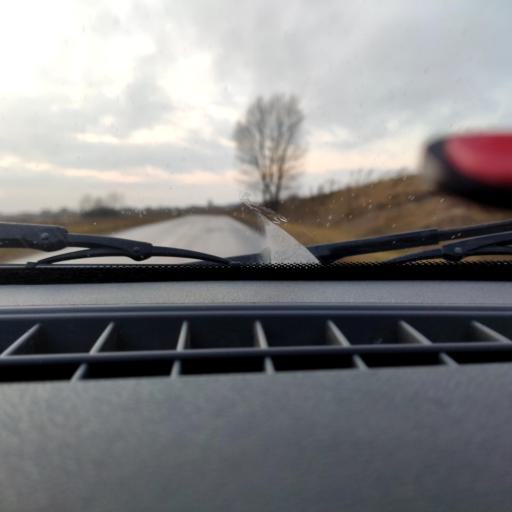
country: RU
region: Bashkortostan
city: Avdon
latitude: 54.5114
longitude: 55.8496
